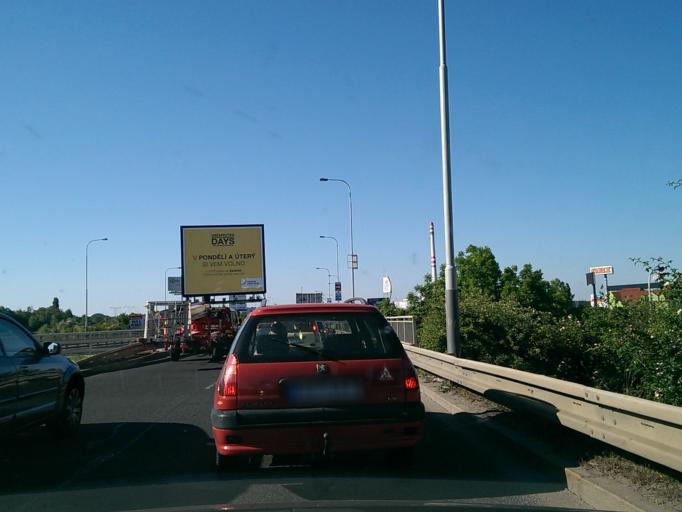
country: CZ
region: Praha
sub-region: Praha 14
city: Hostavice
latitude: 50.0682
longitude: 14.5374
